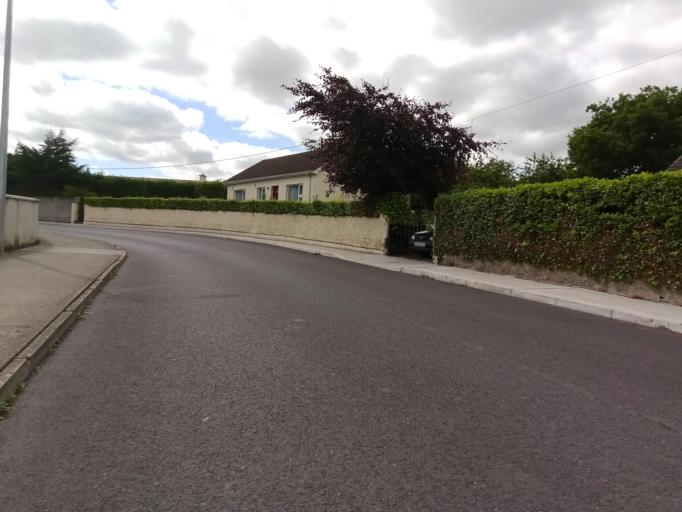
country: IE
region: Leinster
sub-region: Kilkenny
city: Callan
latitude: 52.5423
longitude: -7.3888
